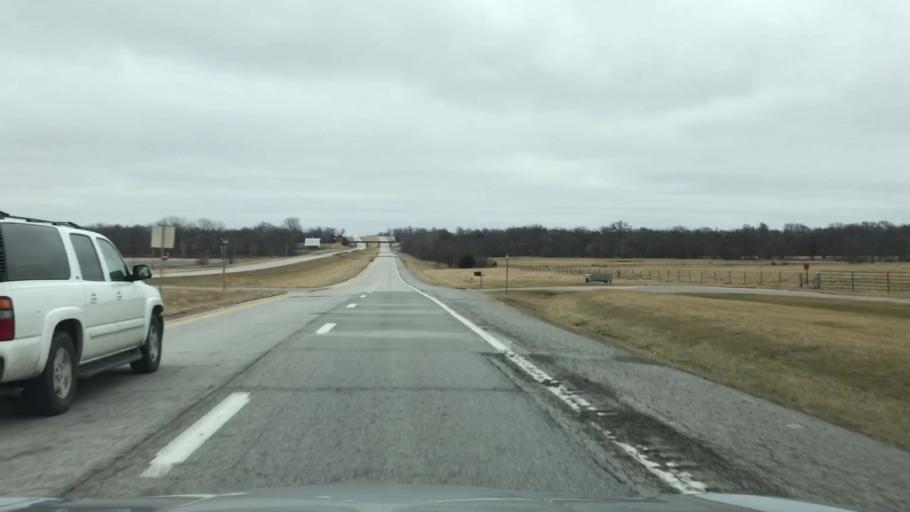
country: US
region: Missouri
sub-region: Linn County
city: Brookfield
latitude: 39.7785
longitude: -93.1547
